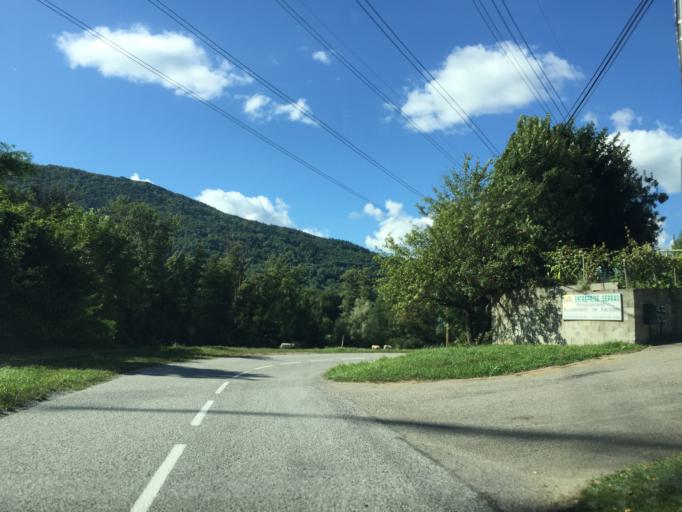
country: FR
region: Rhone-Alpes
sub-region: Departement de la Savoie
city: Coise-Saint-Jean-Pied-Gauthier
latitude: 45.4917
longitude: 6.1588
